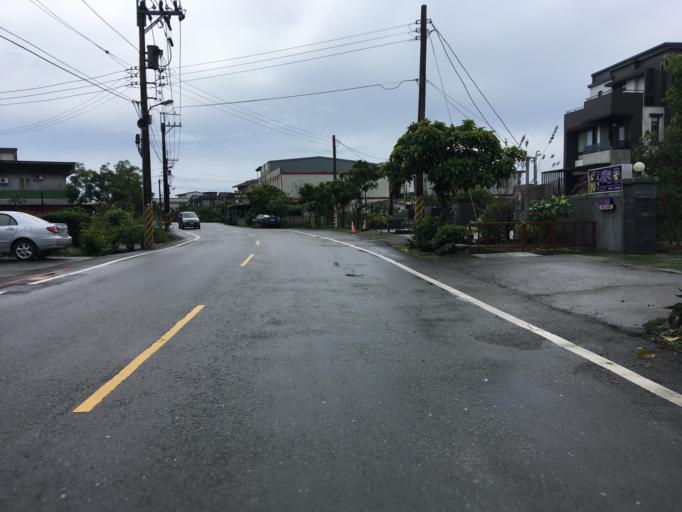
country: TW
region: Taiwan
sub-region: Yilan
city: Yilan
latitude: 24.6680
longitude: 121.7883
